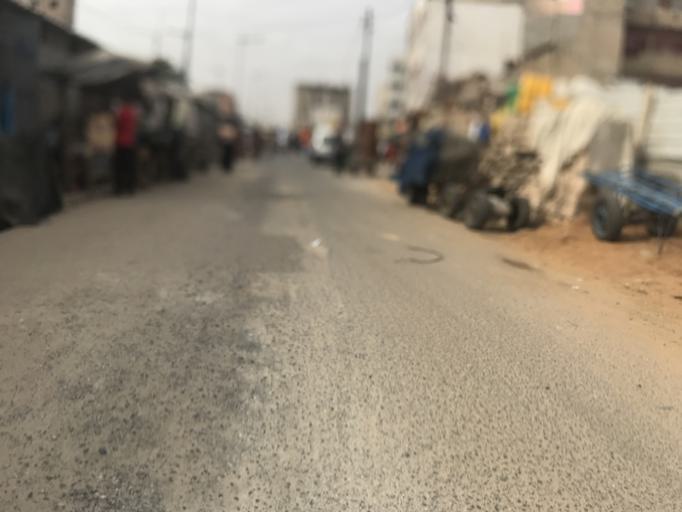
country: SN
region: Dakar
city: Dakar
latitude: 14.6794
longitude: -17.4559
